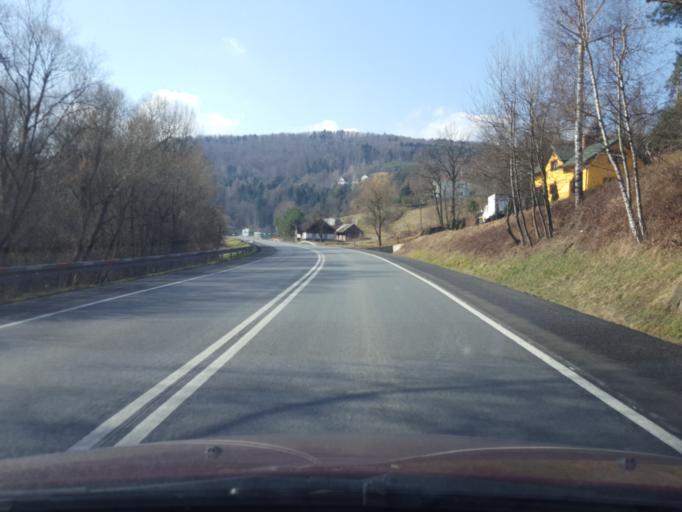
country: PL
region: Lesser Poland Voivodeship
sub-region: Powiat nowosadecki
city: Lososina Dolna
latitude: 49.7828
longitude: 20.6448
